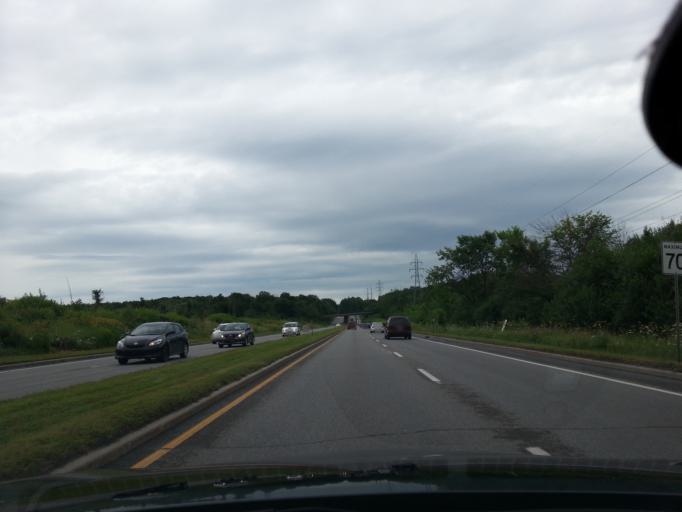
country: CA
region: Quebec
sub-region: Outaouais
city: Gatineau
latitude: 45.4459
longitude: -75.7567
